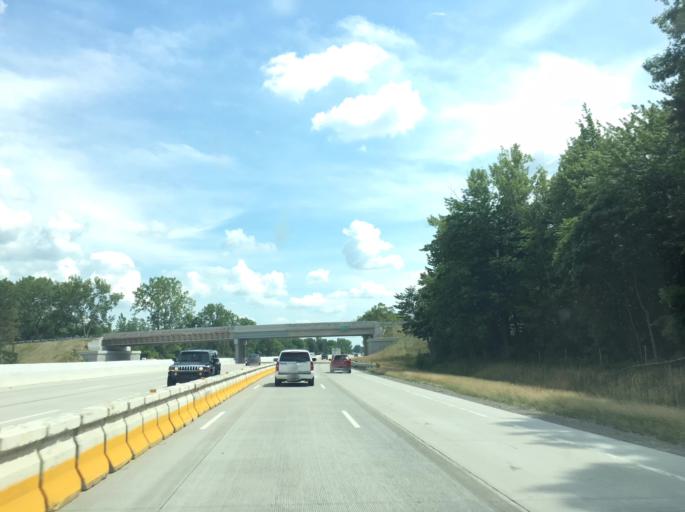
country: US
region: Michigan
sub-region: Saginaw County
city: Bridgeport
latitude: 43.3664
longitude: -83.8682
